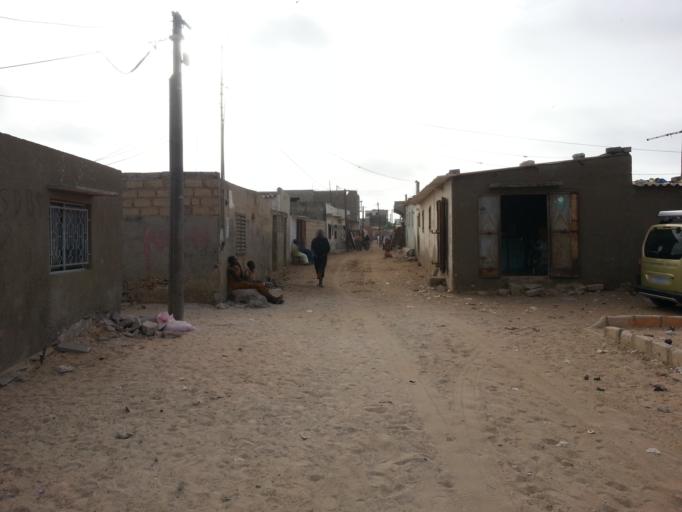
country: SN
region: Dakar
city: Pikine
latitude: 14.7689
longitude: -17.3822
